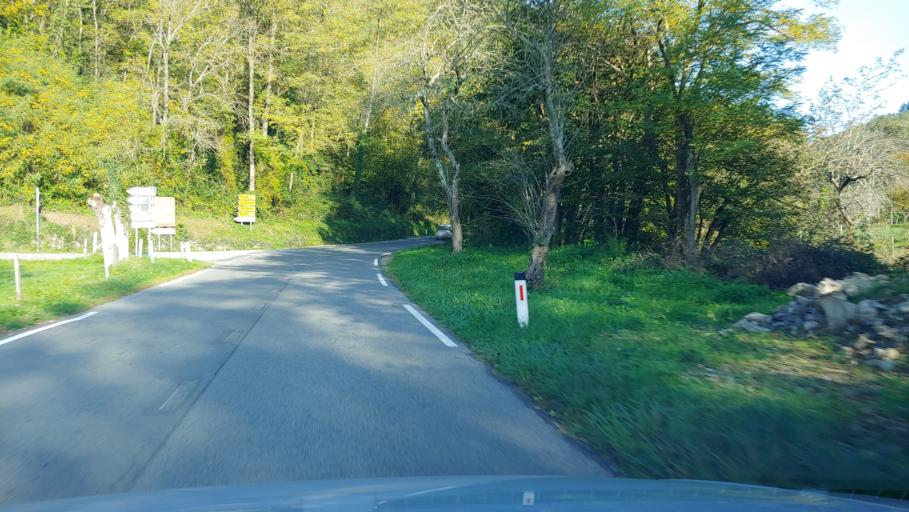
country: SI
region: Ajdovscina
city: Ajdovscina
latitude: 45.8135
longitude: 13.8914
